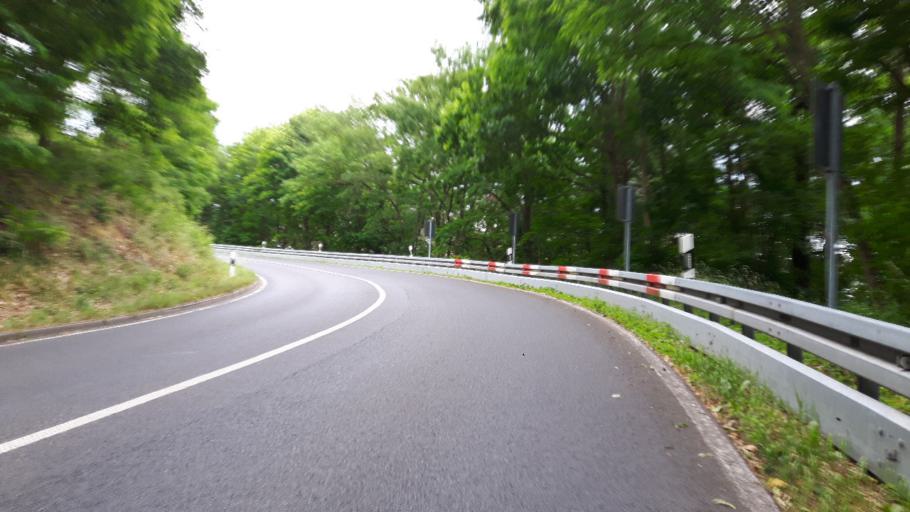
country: DE
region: Brandenburg
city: Liepe
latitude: 52.8620
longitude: 14.0033
